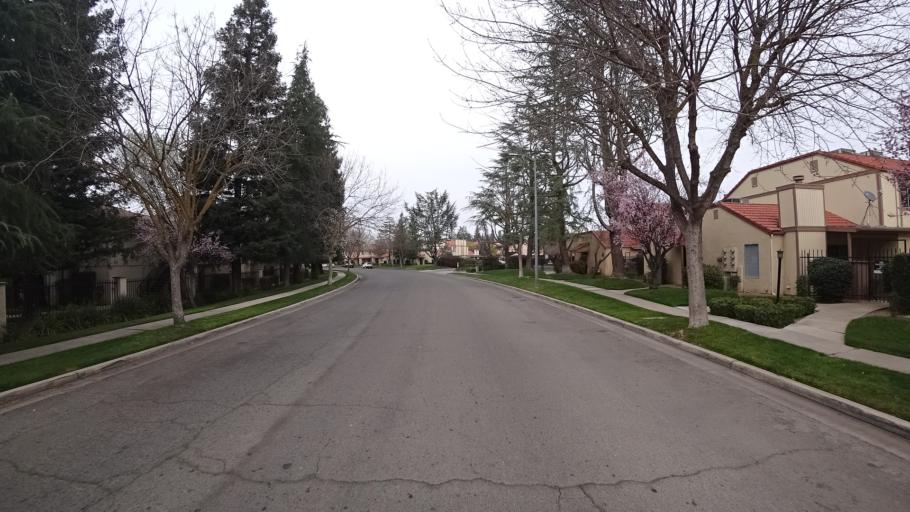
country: US
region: California
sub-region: Fresno County
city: Clovis
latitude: 36.8526
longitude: -119.7991
